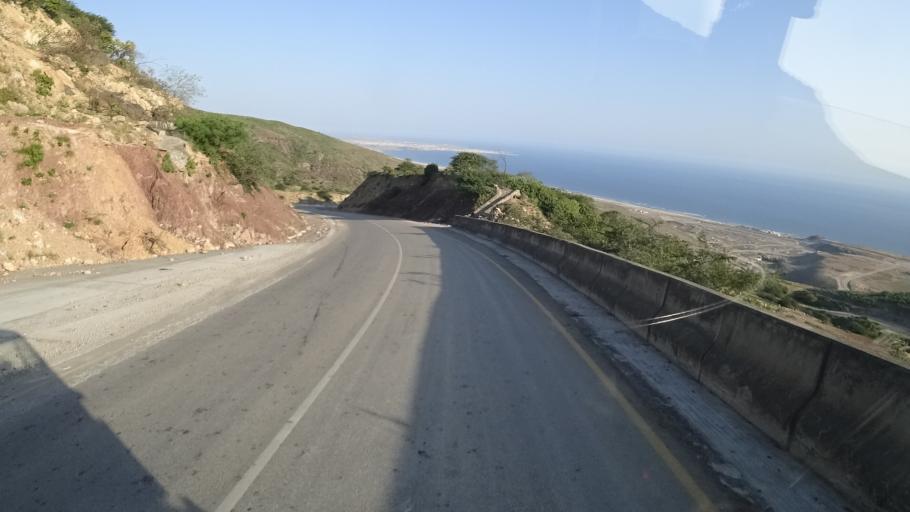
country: OM
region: Zufar
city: Salalah
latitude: 17.0538
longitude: 54.6109
